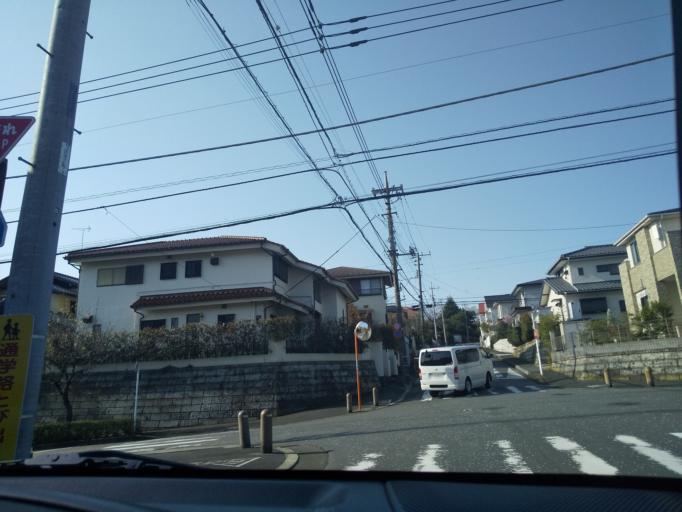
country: JP
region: Tokyo
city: Hino
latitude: 35.6499
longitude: 139.4242
